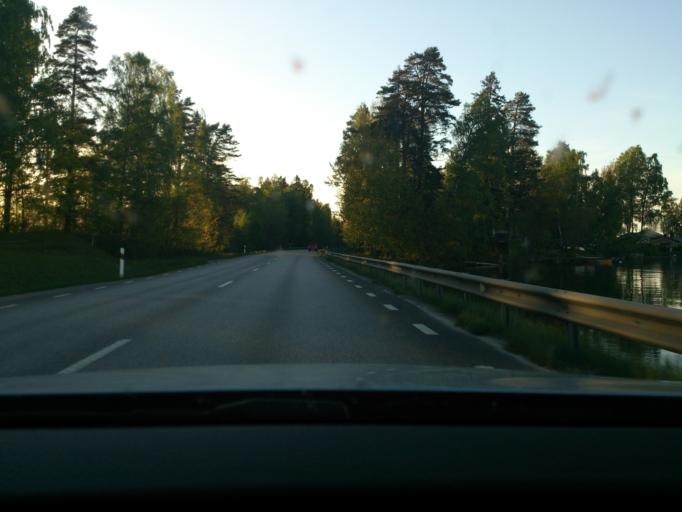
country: SE
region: Kronoberg
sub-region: Vaxjo Kommun
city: Vaexjoe
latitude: 56.9562
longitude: 14.7162
